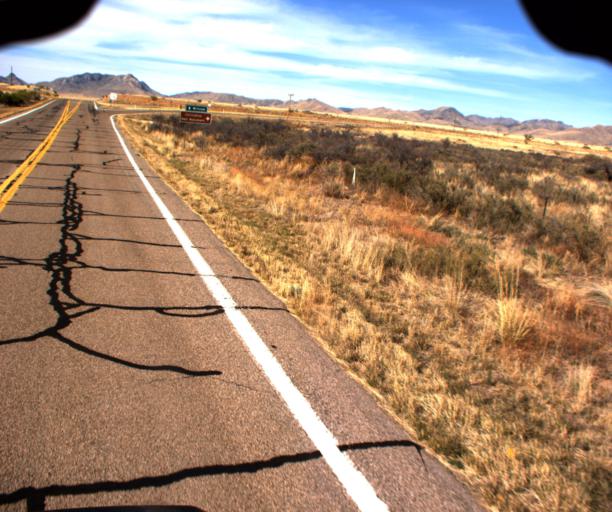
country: US
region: Arizona
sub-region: Cochise County
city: Willcox
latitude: 32.0048
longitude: -109.4400
